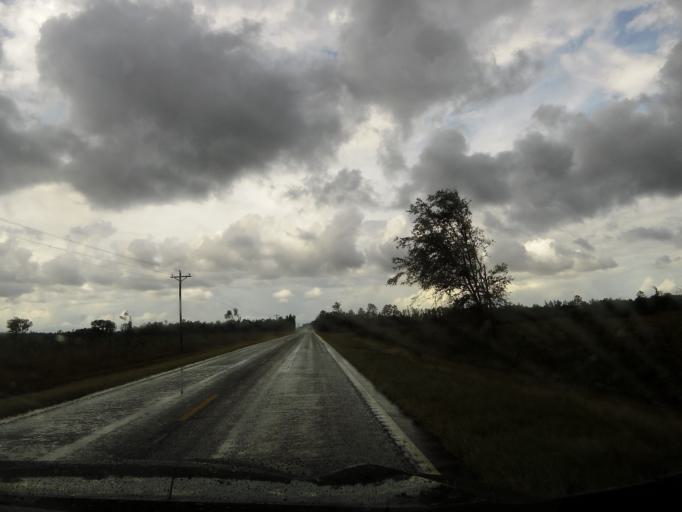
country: US
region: Florida
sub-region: Nassau County
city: Hilliard
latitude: 30.5462
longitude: -82.0407
